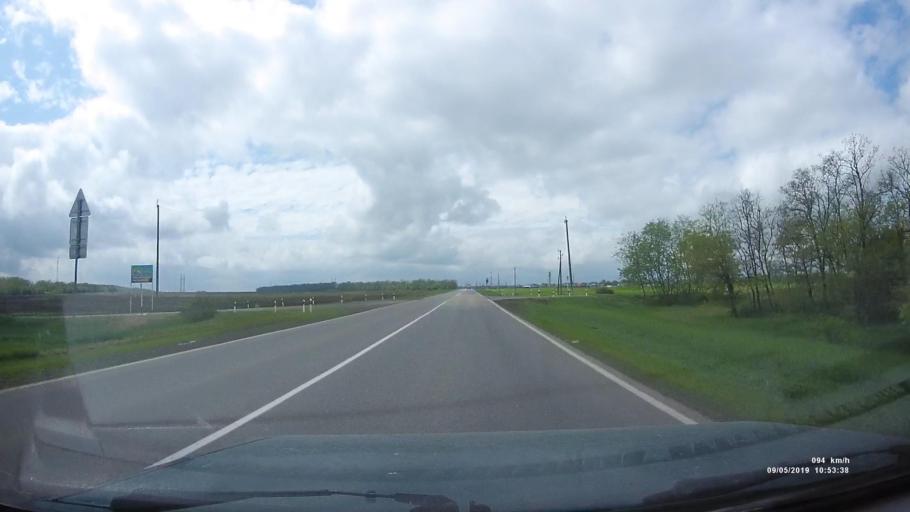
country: RU
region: Rostov
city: Peshkovo
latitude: 46.8859
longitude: 39.3378
